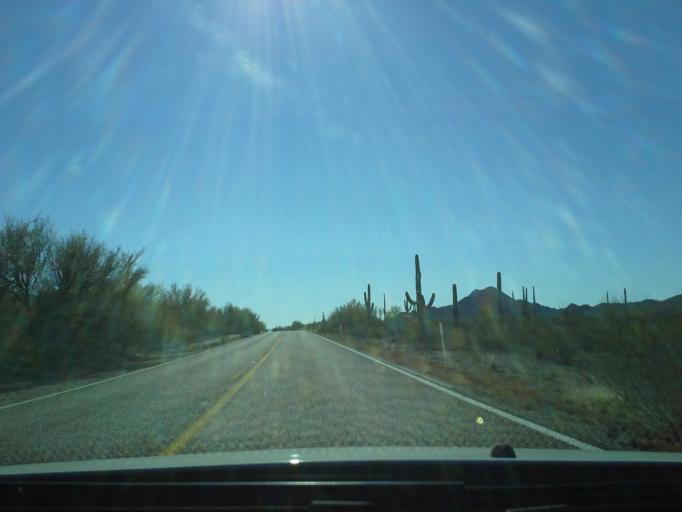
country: MX
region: Sonora
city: Sonoyta
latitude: 31.9978
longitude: -112.8063
